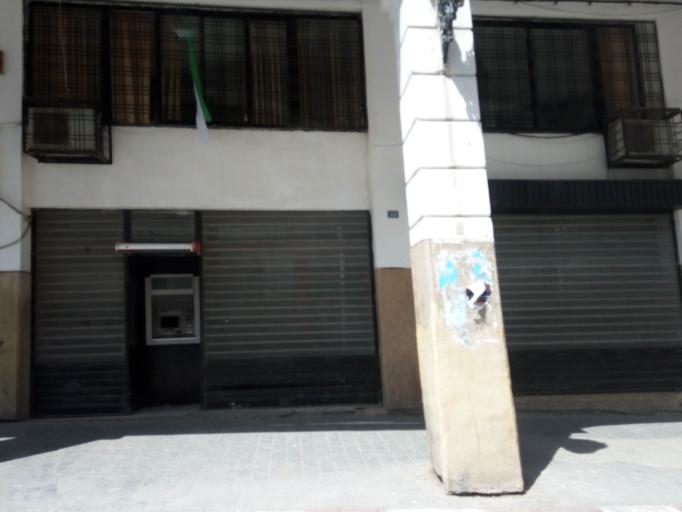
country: DZ
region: Constantine
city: Constantine
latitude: 36.3642
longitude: 6.6055
